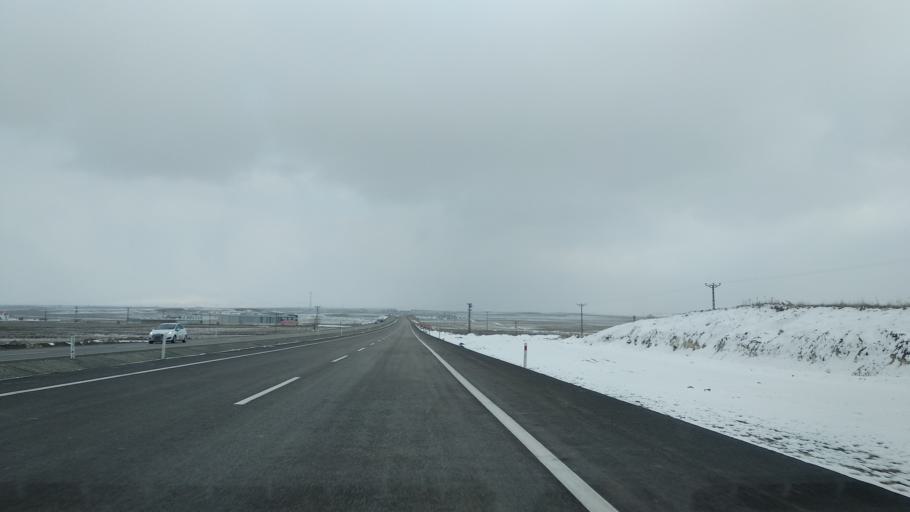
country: TR
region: Kayseri
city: Elbasi
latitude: 38.6538
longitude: 36.0105
